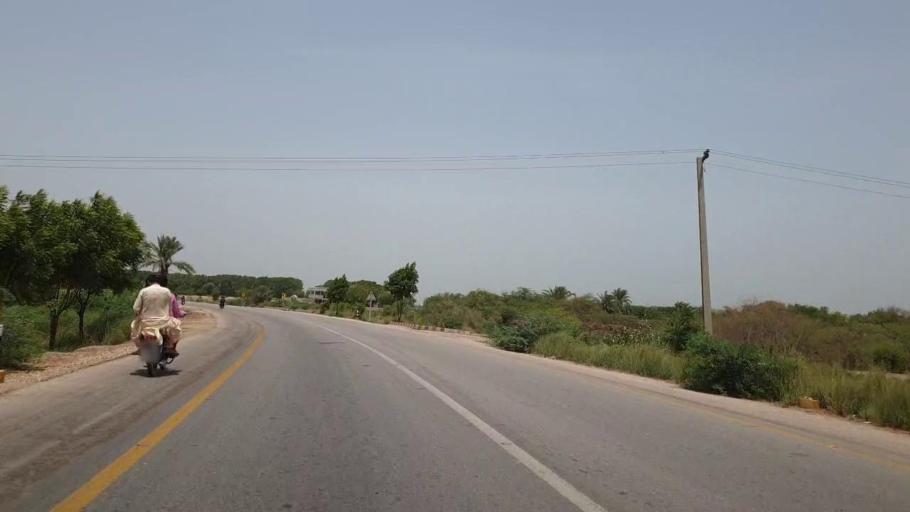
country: PK
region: Sindh
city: Nawabshah
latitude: 26.2459
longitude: 68.4629
